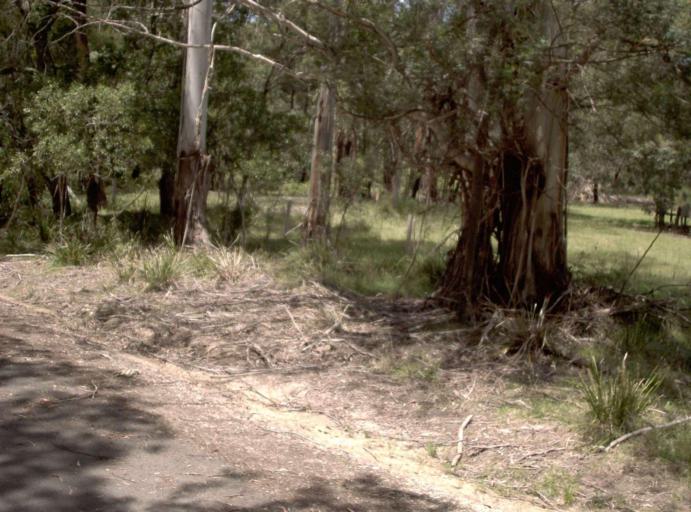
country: AU
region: New South Wales
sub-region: Bombala
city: Bombala
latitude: -37.4268
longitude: 149.0077
